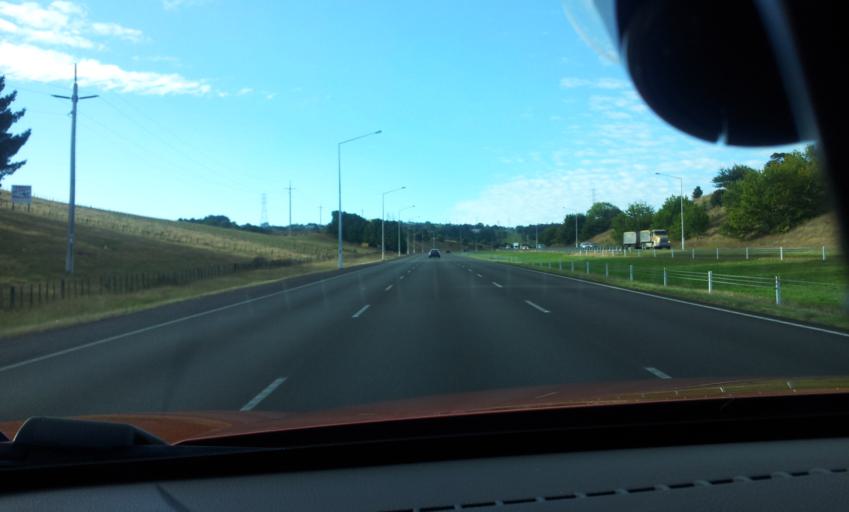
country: NZ
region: Auckland
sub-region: Auckland
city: Pukekohe East
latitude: -37.1619
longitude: 174.9814
